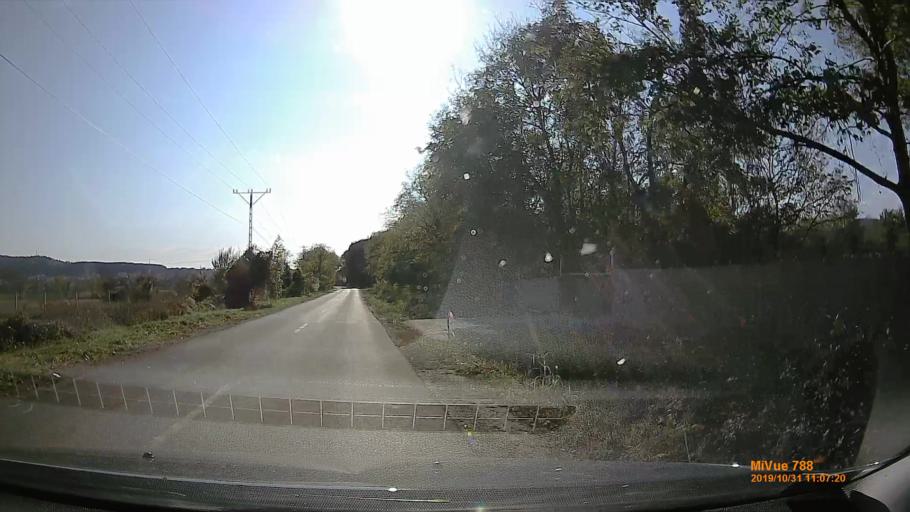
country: HU
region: Pest
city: Pilisborosjeno
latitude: 47.5974
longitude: 18.9988
